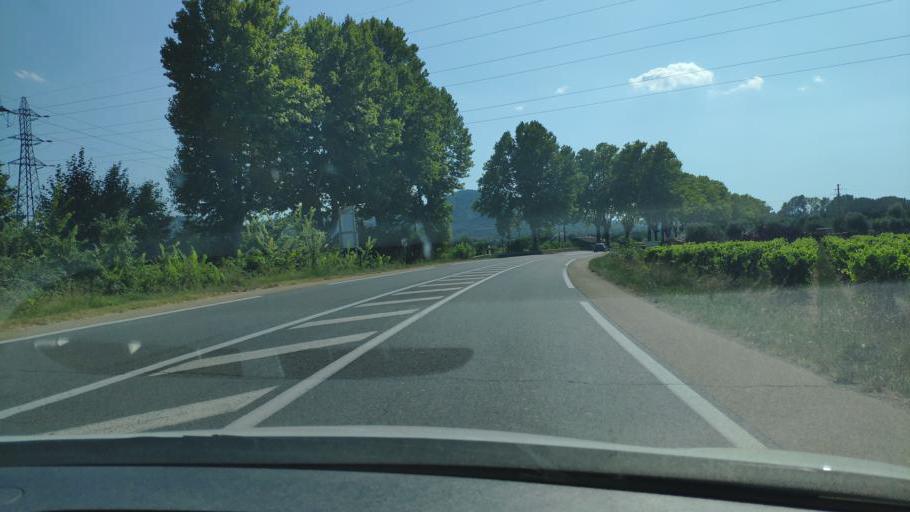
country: FR
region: Provence-Alpes-Cote d'Azur
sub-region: Departement du Var
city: Les Arcs
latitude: 43.4445
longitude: 6.4680
